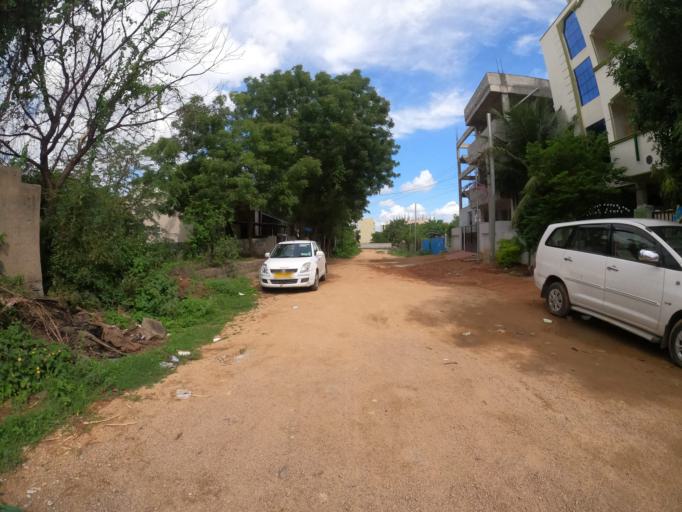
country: IN
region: Telangana
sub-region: Hyderabad
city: Hyderabad
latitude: 17.3535
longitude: 78.3874
